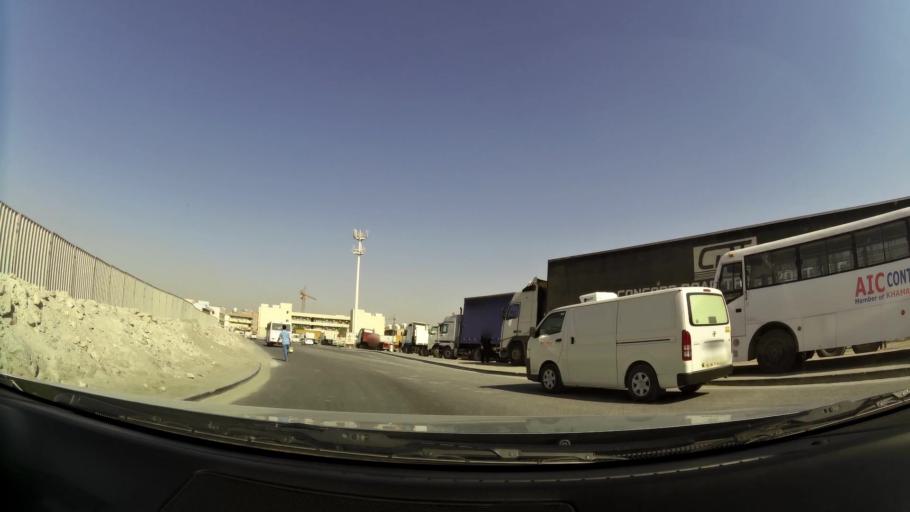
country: AE
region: Dubai
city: Dubai
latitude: 25.0039
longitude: 55.1046
